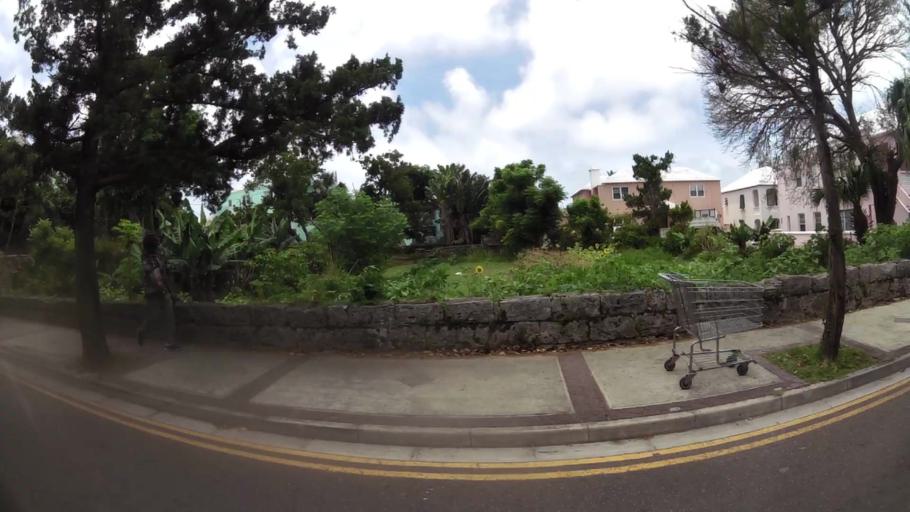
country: BM
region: Hamilton city
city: Hamilton
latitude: 32.2983
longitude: -64.7850
